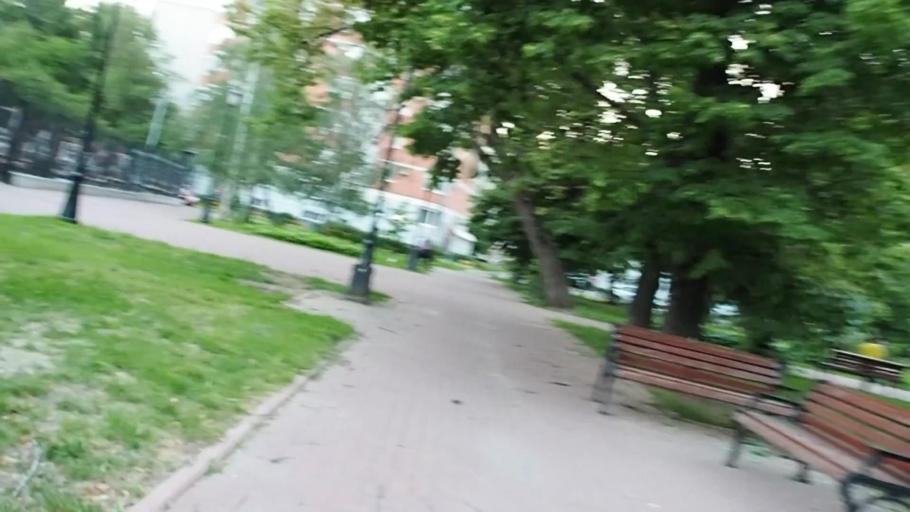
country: RU
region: Moscow
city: Lefortovo
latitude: 55.7855
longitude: 37.6892
